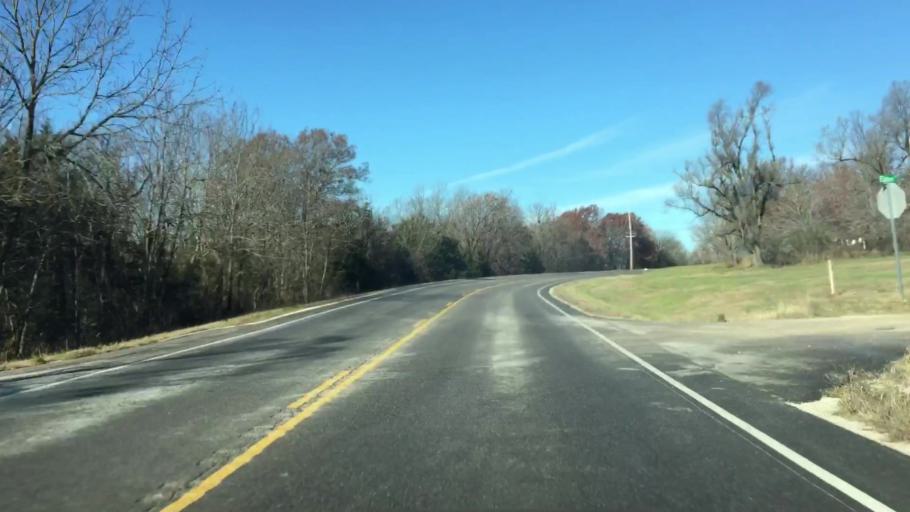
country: US
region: Missouri
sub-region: Miller County
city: Eldon
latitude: 38.3646
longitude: -92.6129
